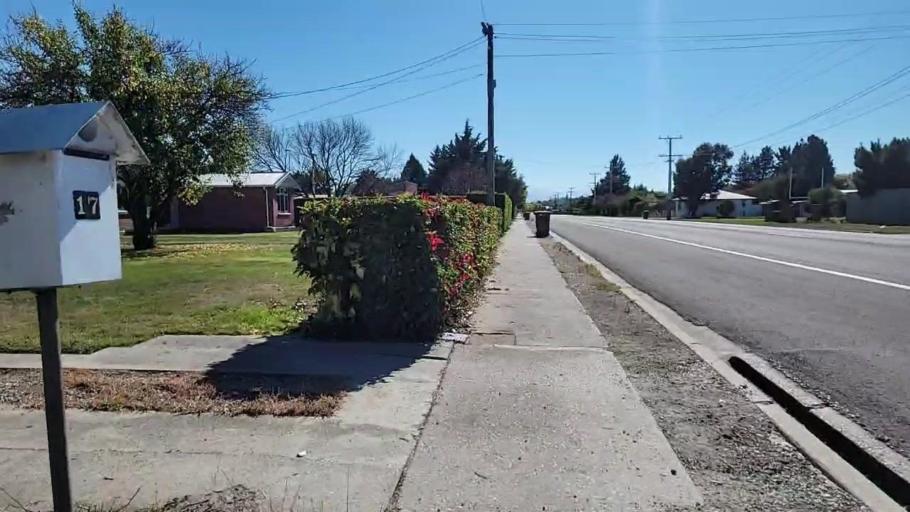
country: NZ
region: Otago
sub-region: Queenstown-Lakes District
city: Wanaka
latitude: -45.1027
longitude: 169.5956
